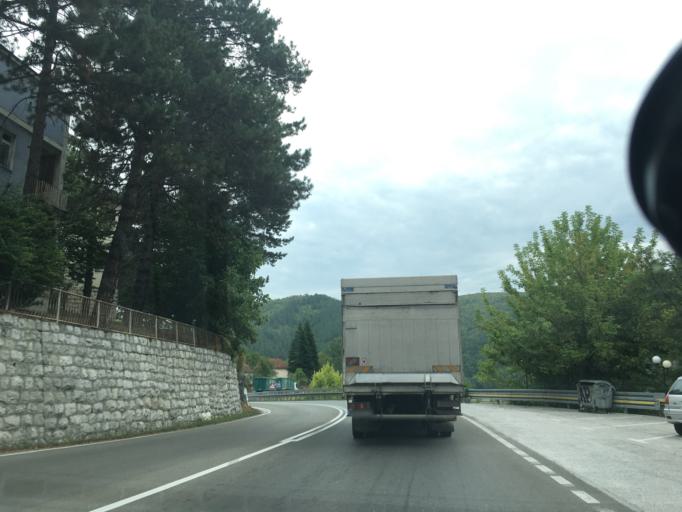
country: RS
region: Central Serbia
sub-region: Moravicki Okrug
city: Lucani
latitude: 43.9111
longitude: 20.2328
